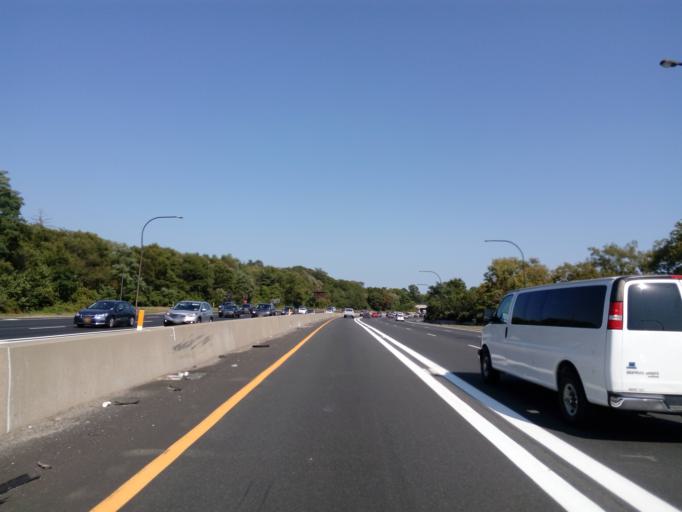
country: US
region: New York
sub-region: Nassau County
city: East Hills
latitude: 40.7834
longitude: -73.6201
